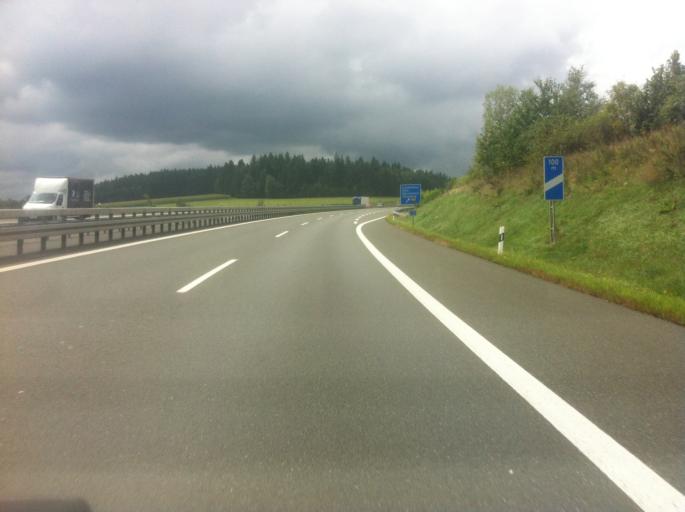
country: DE
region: Bavaria
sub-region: Upper Palatinate
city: Leuchtenberg
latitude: 49.5782
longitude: 12.2752
